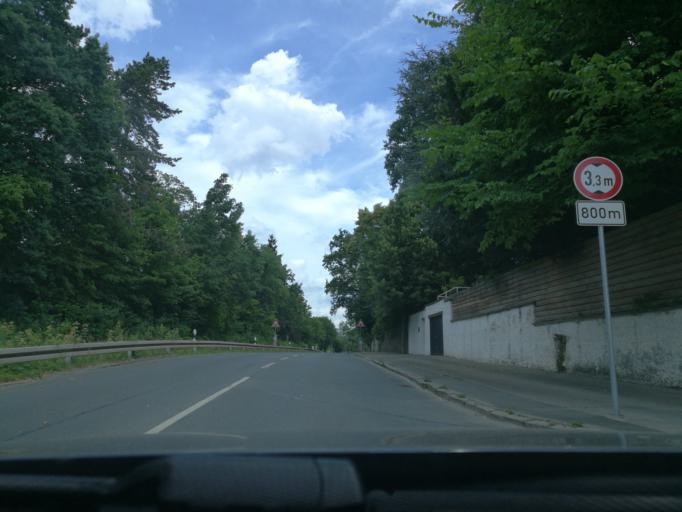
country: DE
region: Bavaria
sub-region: Regierungsbezirk Mittelfranken
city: Furth
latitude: 49.4640
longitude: 10.9701
